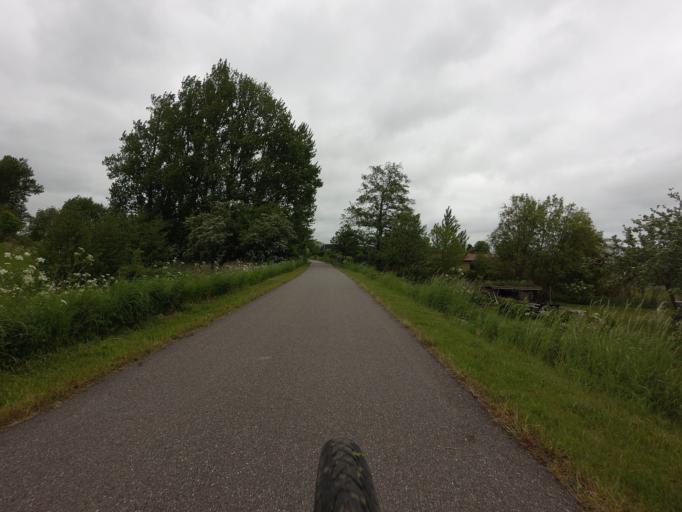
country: DK
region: Zealand
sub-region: Slagelse Kommune
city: Skaelskor
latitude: 55.2456
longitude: 11.3054
